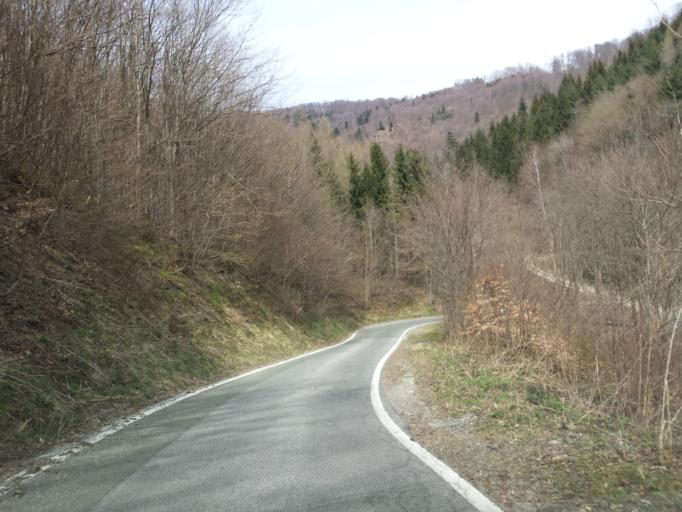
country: HR
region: Grad Zagreb
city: Kasina
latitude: 45.8847
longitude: 15.9430
